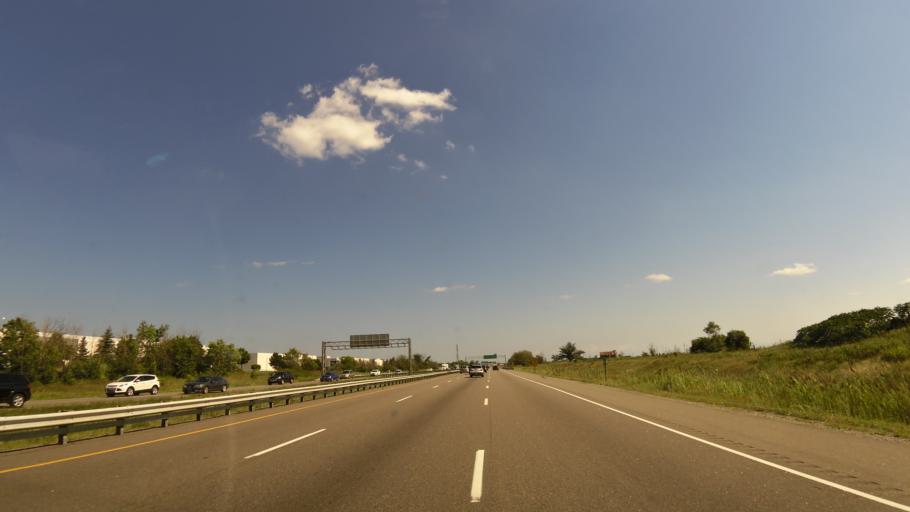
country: CA
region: Ontario
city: Oakville
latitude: 43.5185
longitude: -79.7064
